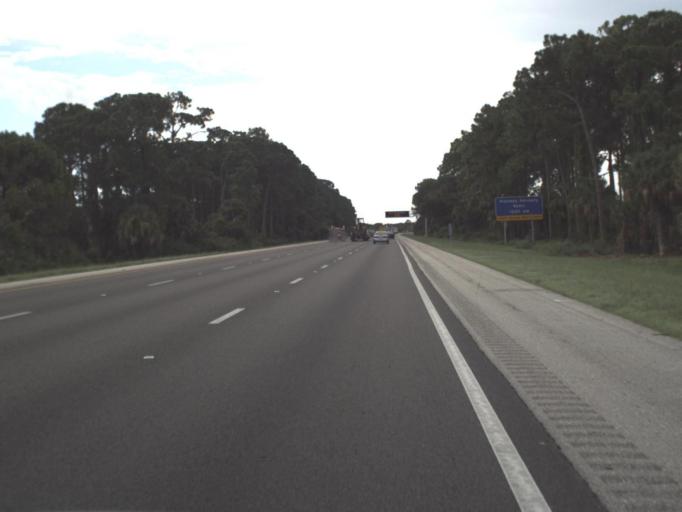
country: US
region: Florida
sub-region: Sarasota County
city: Osprey
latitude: 27.2179
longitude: -82.4479
